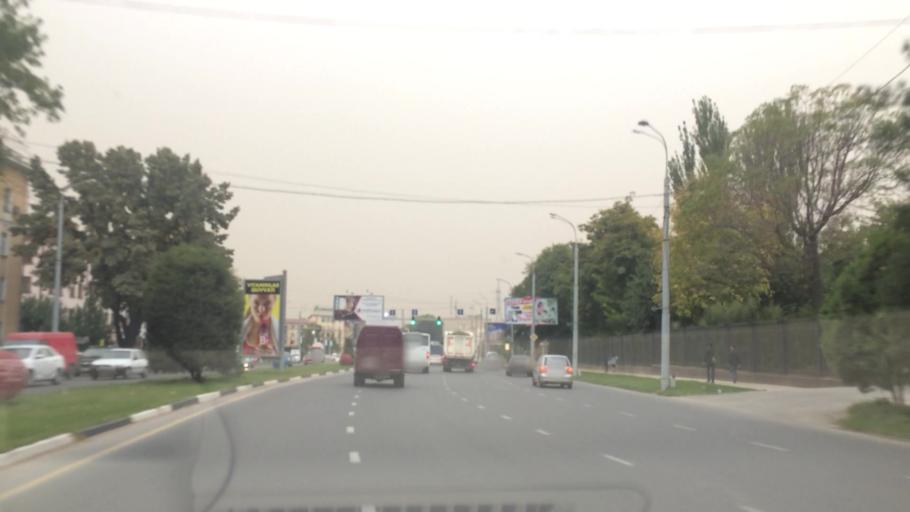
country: UZ
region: Toshkent Shahri
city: Tashkent
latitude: 41.3033
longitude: 69.2479
